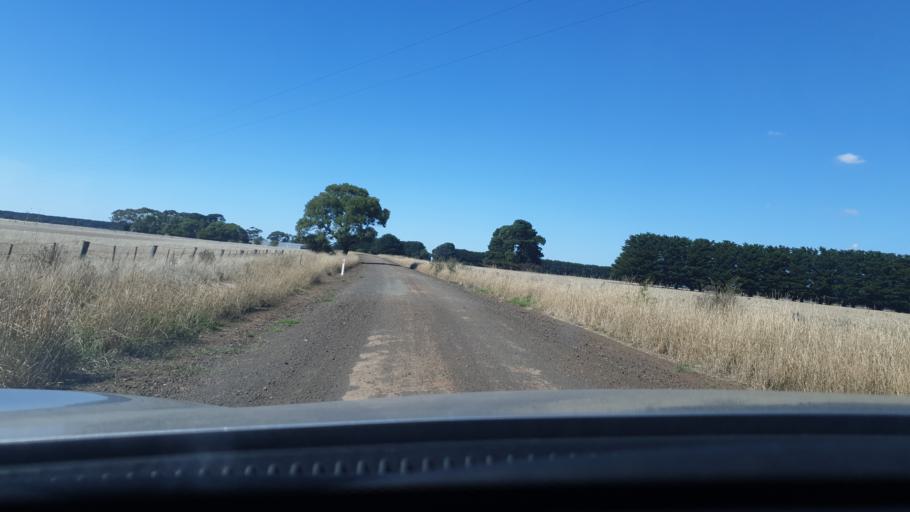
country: AU
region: Victoria
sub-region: Warrnambool
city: Warrnambool
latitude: -38.1658
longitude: 142.3692
